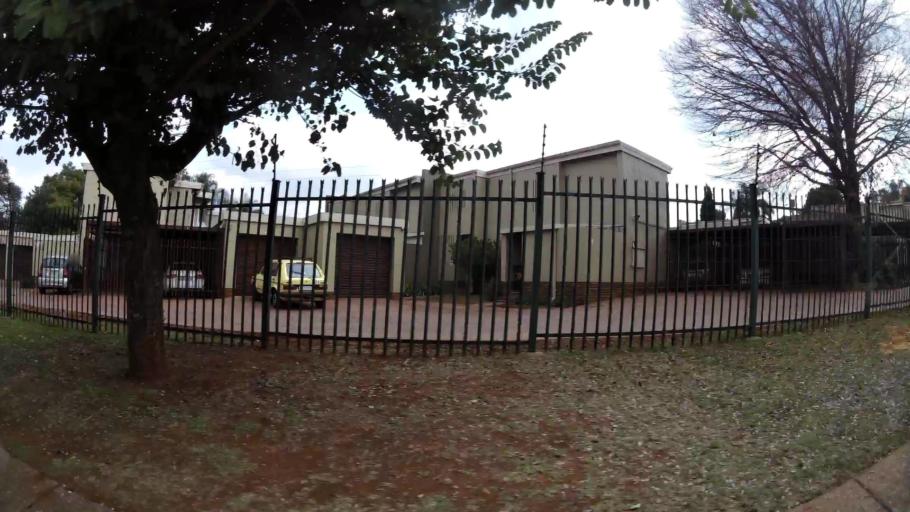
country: ZA
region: Gauteng
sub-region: City of Tshwane Metropolitan Municipality
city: Pretoria
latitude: -25.7504
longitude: 28.3142
